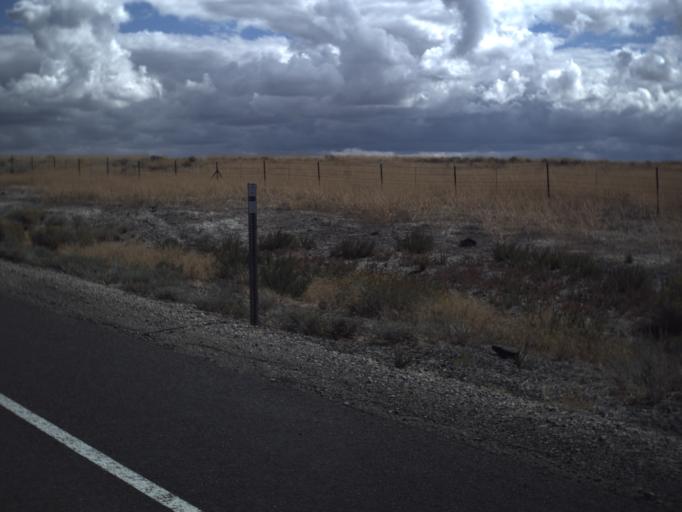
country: US
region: Utah
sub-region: Tooele County
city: Wendover
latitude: 40.7262
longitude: -113.2610
